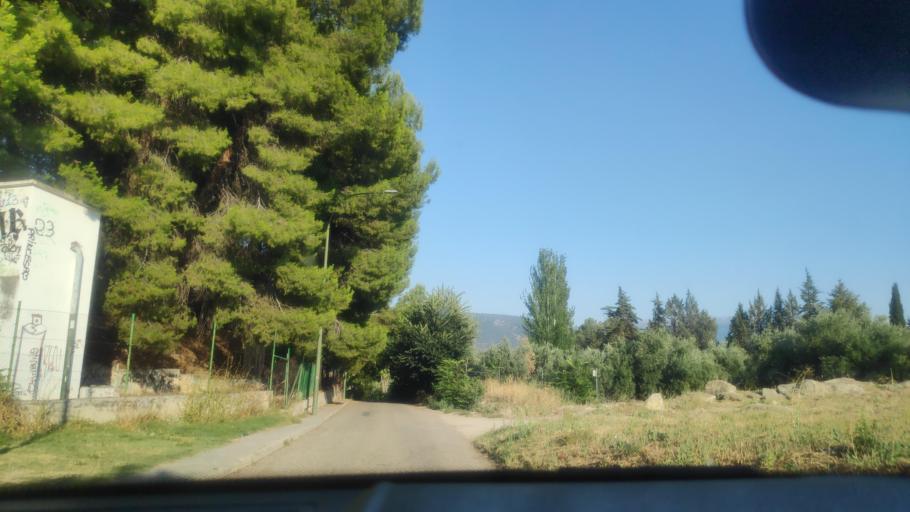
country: ES
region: Andalusia
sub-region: Provincia de Jaen
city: Jaen
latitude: 37.7673
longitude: -3.7791
